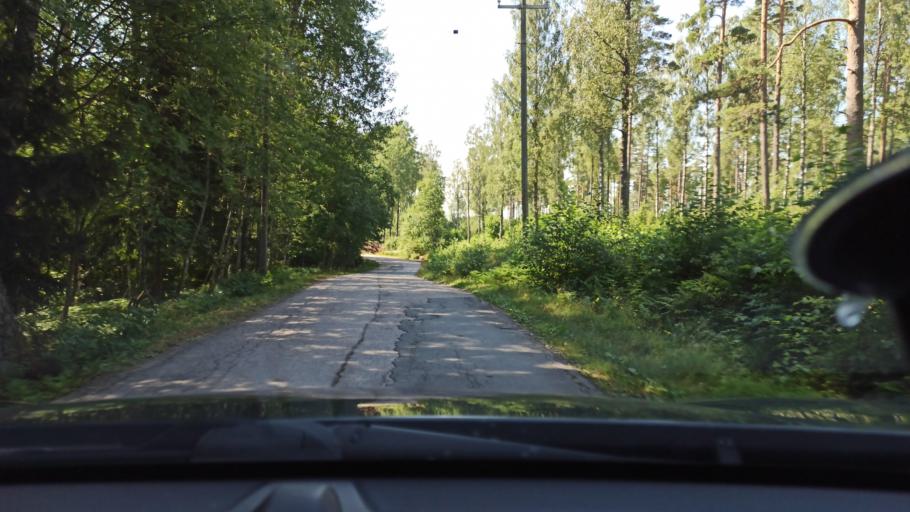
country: FI
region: Uusimaa
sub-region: Helsinki
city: Espoo
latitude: 60.1518
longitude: 24.5669
